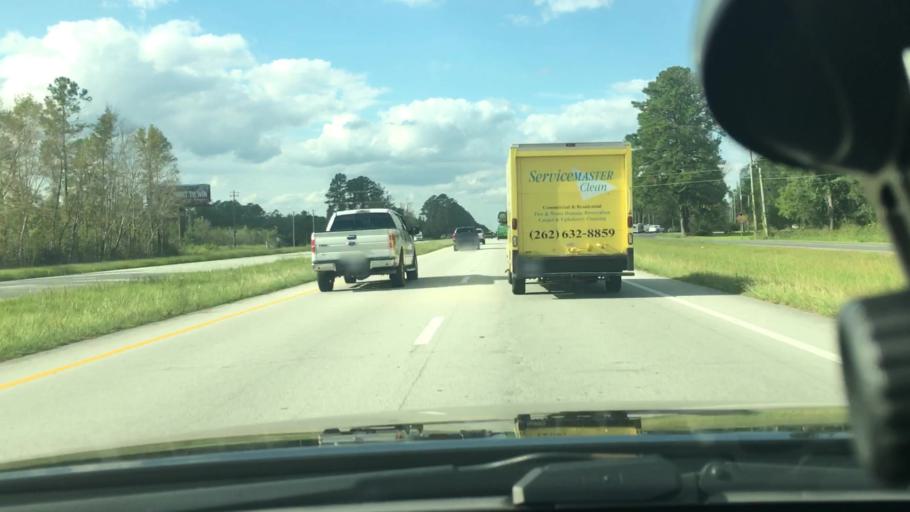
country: US
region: North Carolina
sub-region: Craven County
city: Neuse Forest
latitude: 35.0119
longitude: -76.9929
